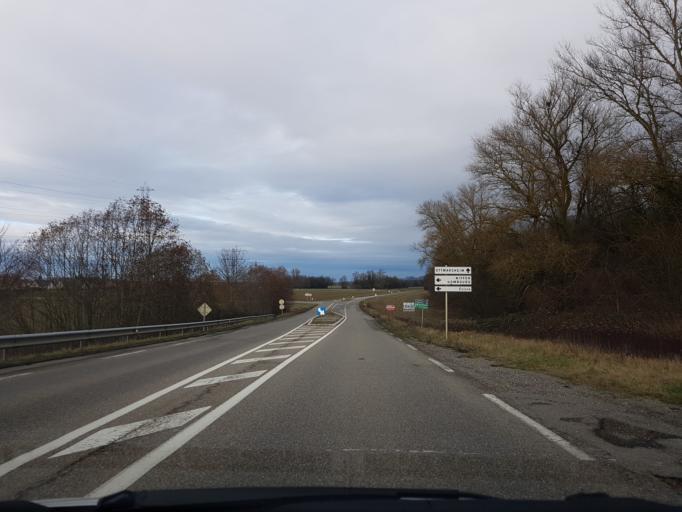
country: FR
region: Alsace
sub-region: Departement du Haut-Rhin
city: Kembs
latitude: 47.7071
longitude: 7.5106
